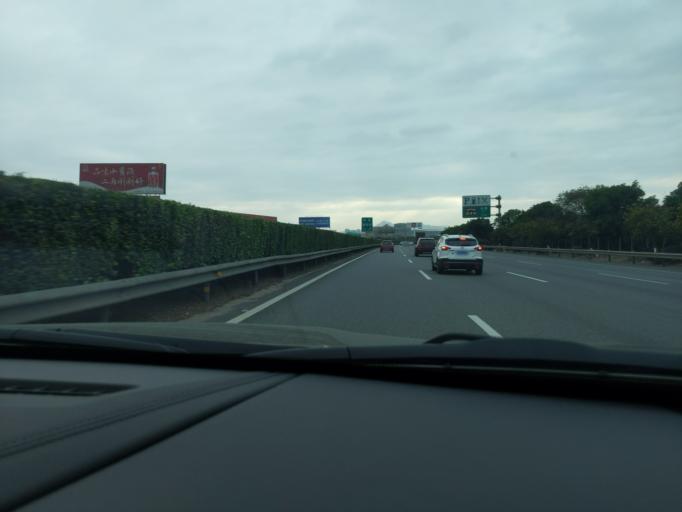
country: CN
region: Fujian
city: Neikeng
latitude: 24.7583
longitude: 118.4460
